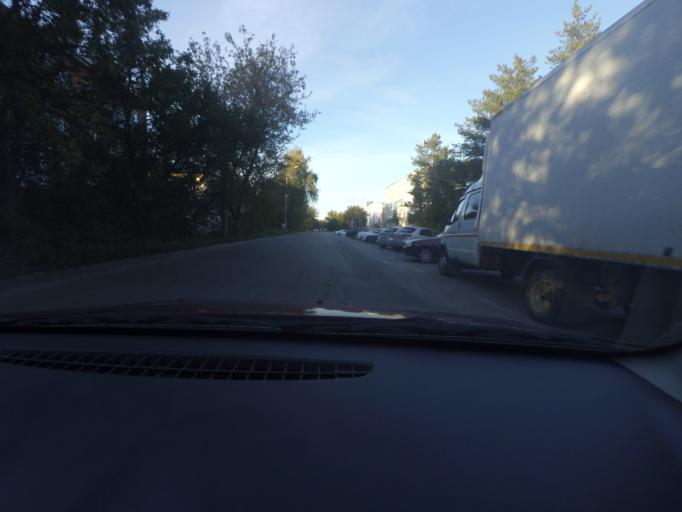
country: RU
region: Nizjnij Novgorod
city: Nizhniy Novgorod
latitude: 56.2873
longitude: 43.9947
